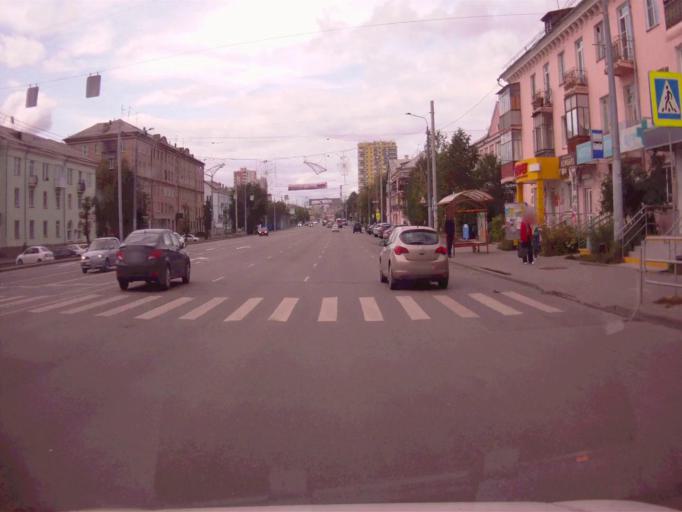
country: RU
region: Chelyabinsk
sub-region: Gorod Chelyabinsk
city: Chelyabinsk
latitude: 55.1417
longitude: 61.3933
